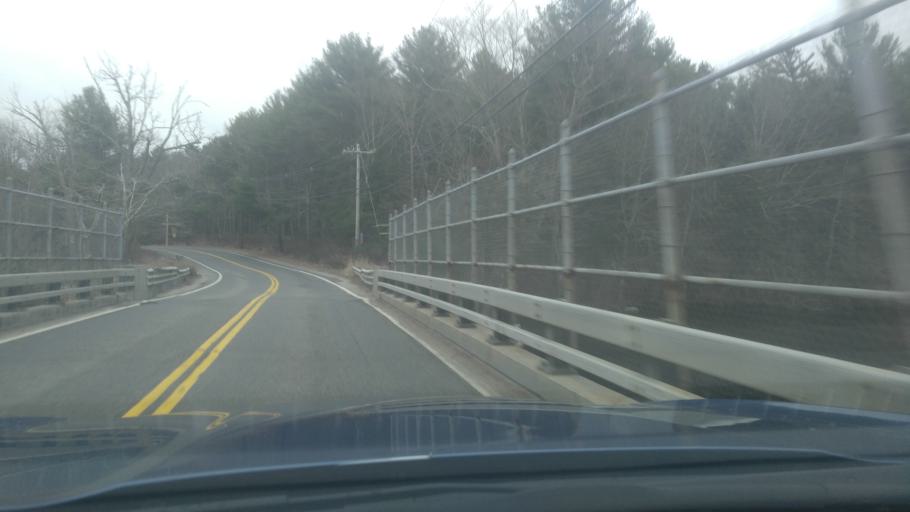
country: US
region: Rhode Island
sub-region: Kent County
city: West Greenwich
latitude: 41.6653
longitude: -71.6193
